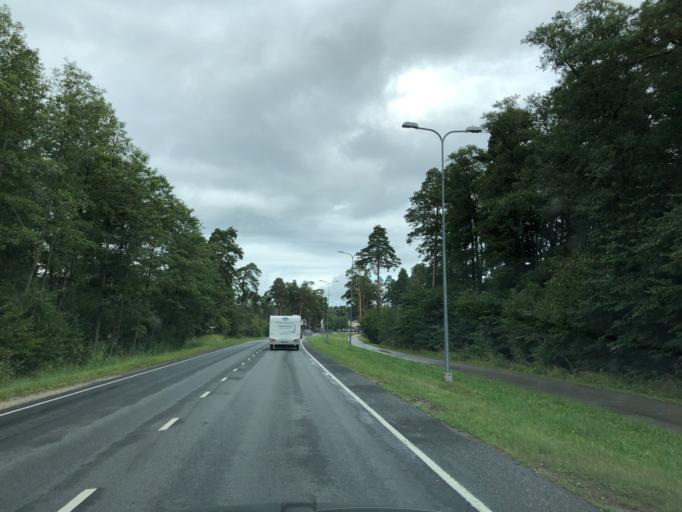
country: EE
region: Laeaene
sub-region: Haapsalu linn
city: Haapsalu
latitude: 58.9273
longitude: 23.5250
